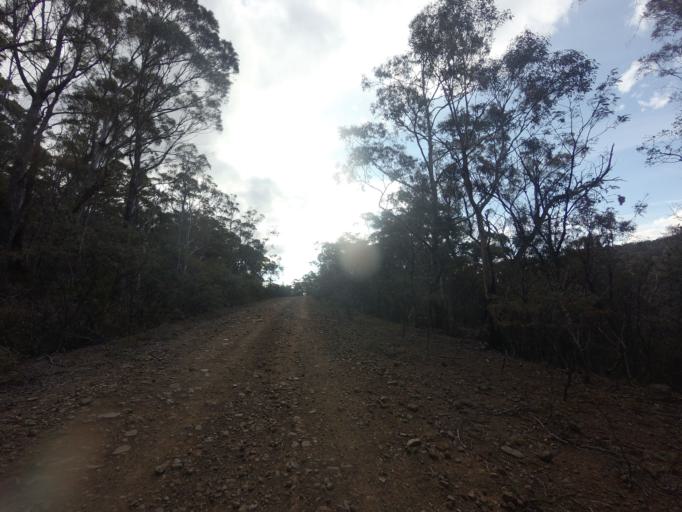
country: AU
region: Tasmania
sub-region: Break O'Day
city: St Helens
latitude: -41.8548
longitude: 148.0378
